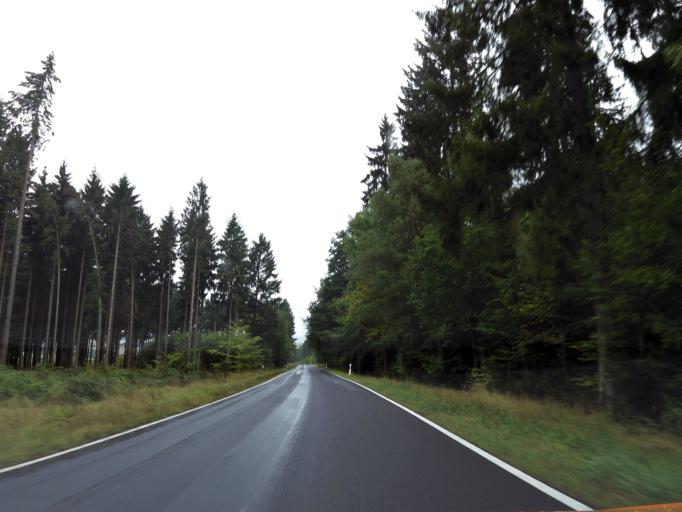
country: DE
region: Rheinland-Pfalz
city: Rayerschied
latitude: 50.0082
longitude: 7.5878
